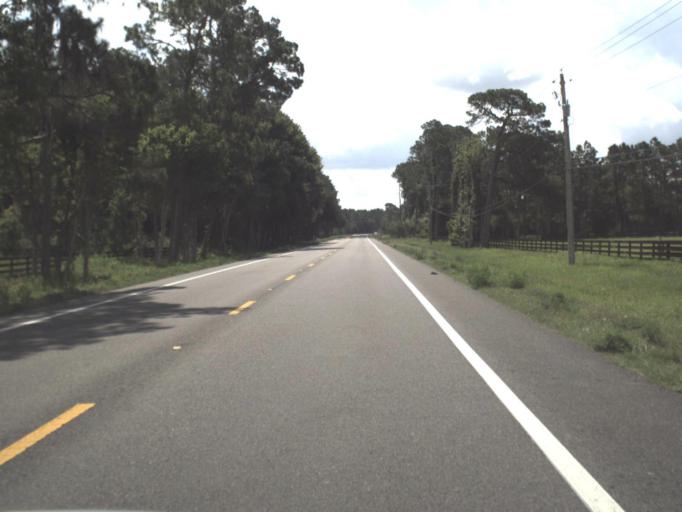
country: US
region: Florida
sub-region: Clay County
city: Green Cove Springs
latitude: 29.9783
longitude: -81.5496
